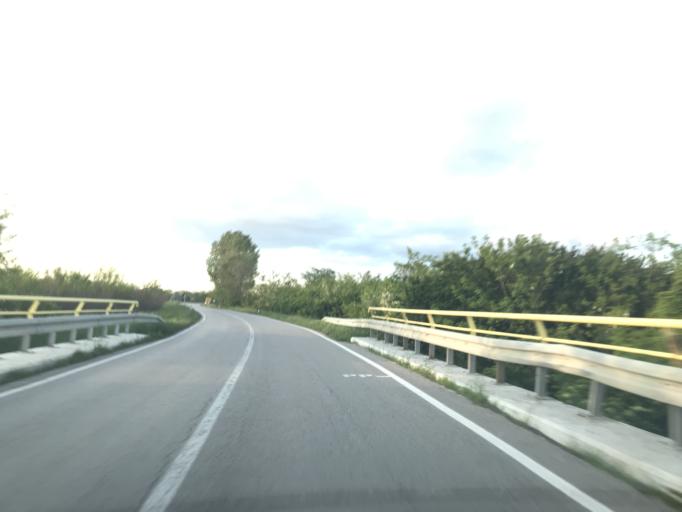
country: RS
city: Cestereg
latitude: 45.5549
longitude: 20.5229
